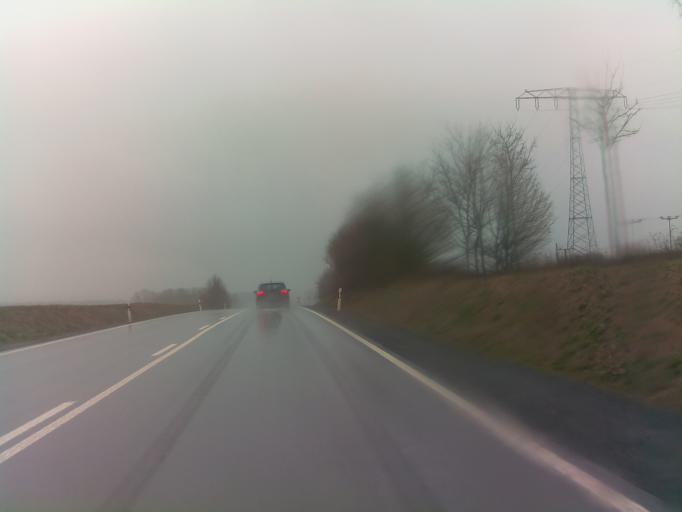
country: DE
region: Thuringia
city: Eisfeld
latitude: 50.4354
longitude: 10.9017
